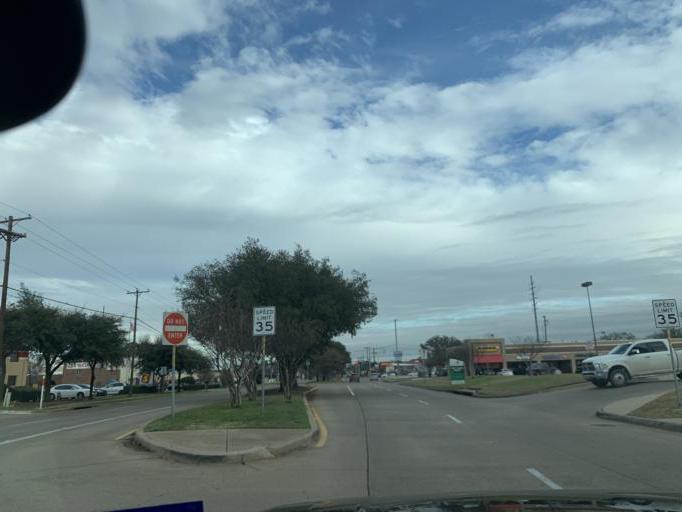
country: US
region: Texas
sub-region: Dallas County
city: Cedar Hill
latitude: 32.5899
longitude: -96.9445
